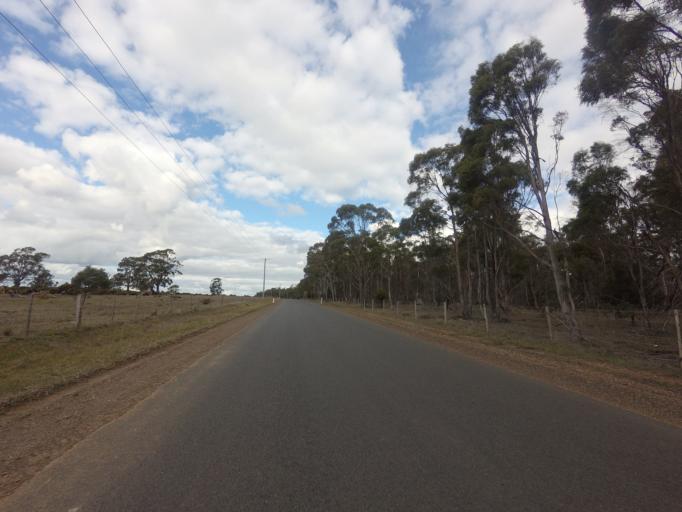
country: AU
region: Tasmania
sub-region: Northern Midlands
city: Longford
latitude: -41.7994
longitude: 147.1292
